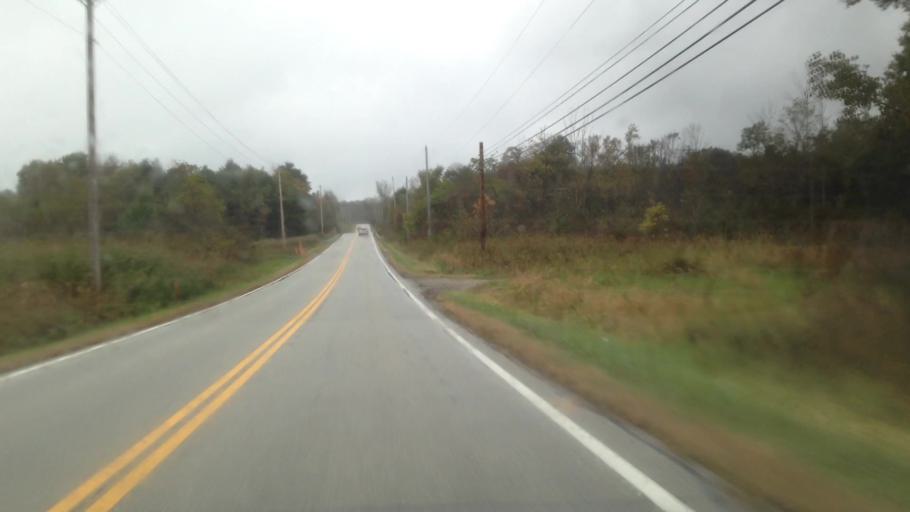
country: US
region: Ohio
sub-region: Summit County
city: Hudson
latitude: 41.2604
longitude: -81.4728
